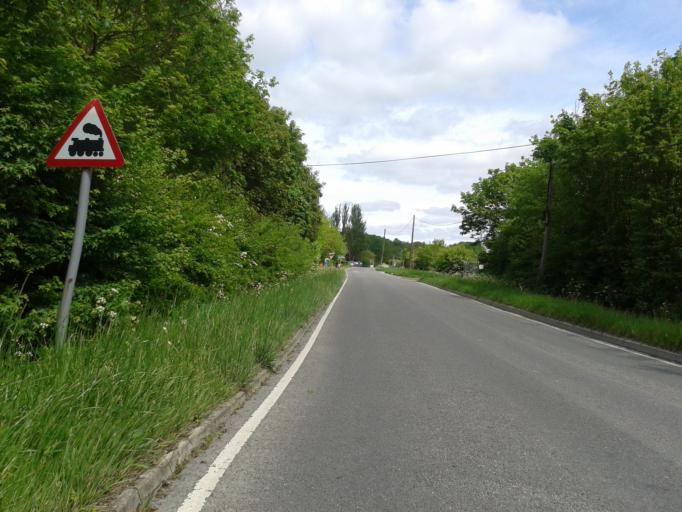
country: GB
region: England
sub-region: Cambridgeshire
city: Haslingfield
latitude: 52.1345
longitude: 0.0403
